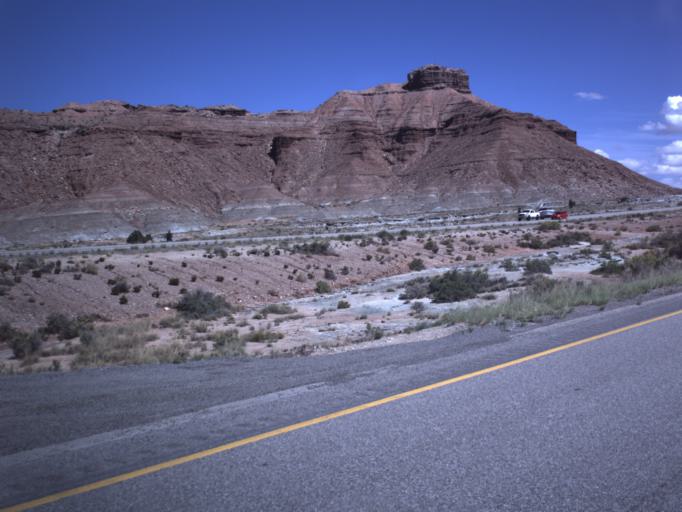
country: US
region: Utah
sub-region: Emery County
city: Ferron
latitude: 38.8310
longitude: -111.1258
